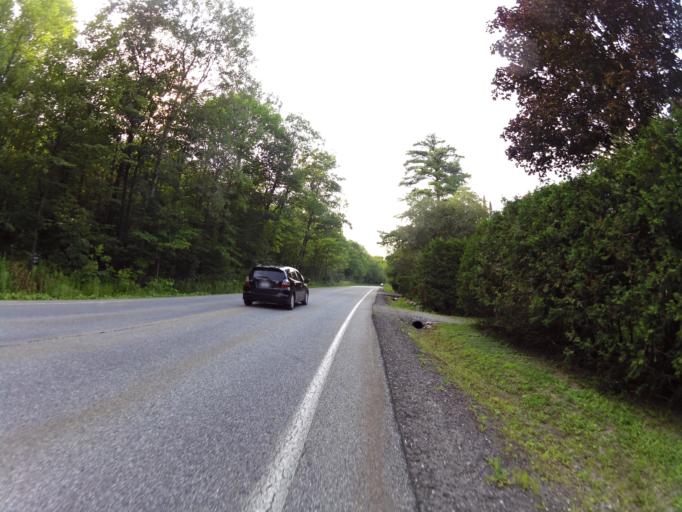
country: CA
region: Quebec
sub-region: Outaouais
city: Gatineau
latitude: 45.4779
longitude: -75.7930
